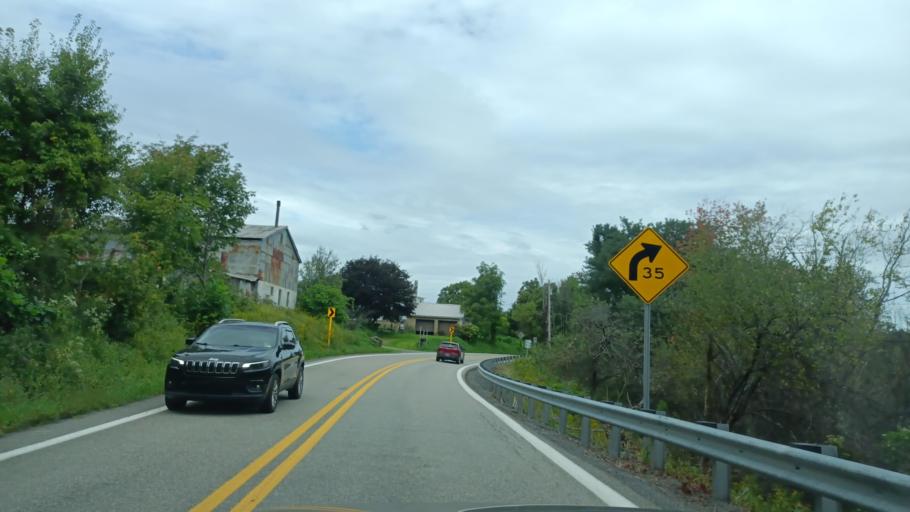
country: US
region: West Virginia
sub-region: Preston County
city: Kingwood
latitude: 39.3290
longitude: -79.7595
